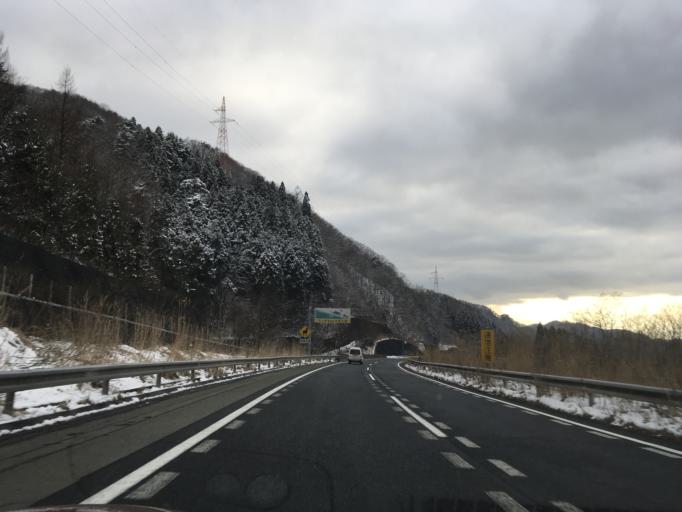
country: JP
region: Yamagata
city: Yamagata-shi
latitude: 38.2241
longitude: 140.4448
